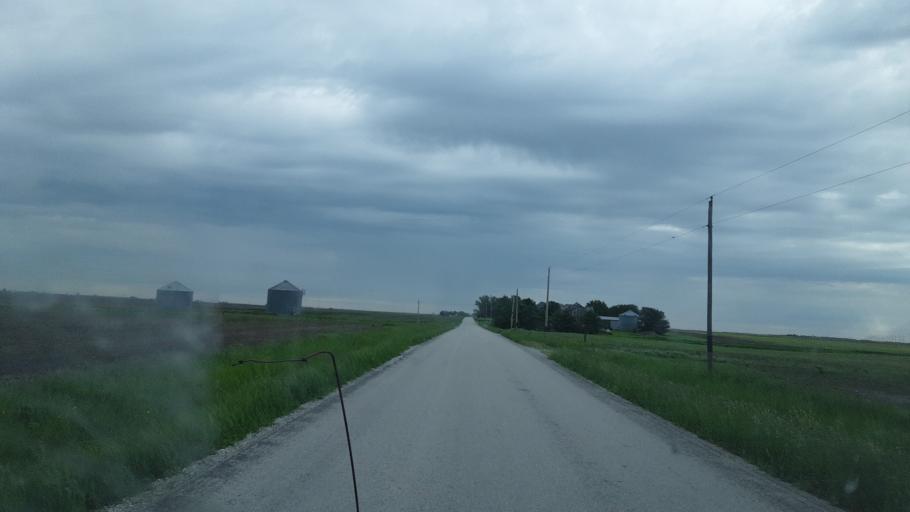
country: US
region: Illinois
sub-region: McDonough County
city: Macomb
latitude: 40.3810
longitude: -90.5213
